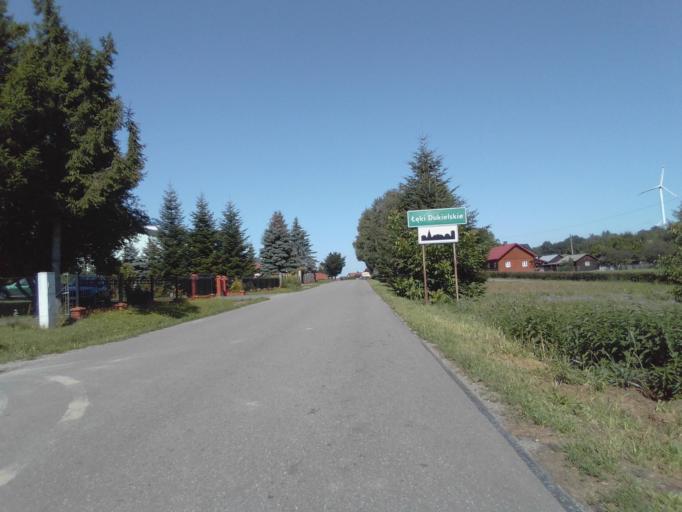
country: PL
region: Subcarpathian Voivodeship
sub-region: Powiat krosnienski
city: Dukla
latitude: 49.6011
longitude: 21.6872
